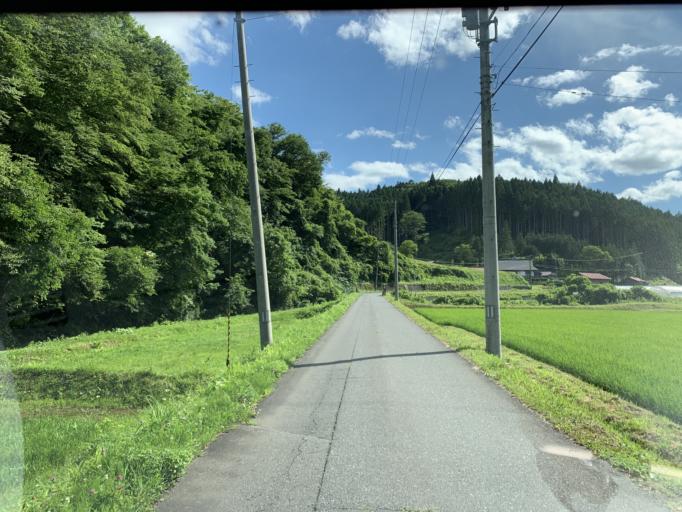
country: JP
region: Iwate
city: Ichinoseki
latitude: 38.9189
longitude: 140.9915
